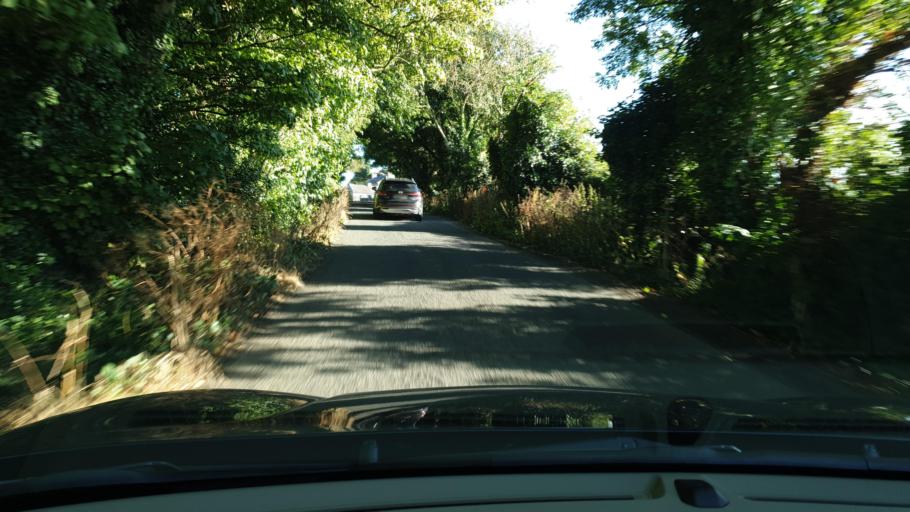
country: IE
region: Leinster
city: Balrothery
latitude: 53.5689
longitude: -6.1999
